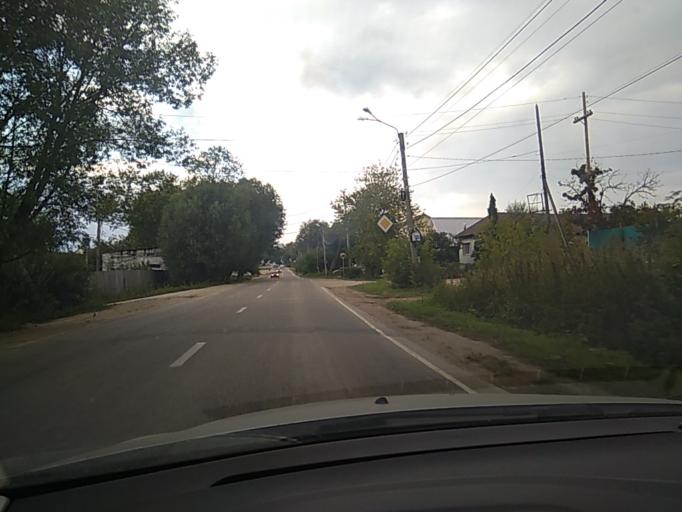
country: RU
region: Chelyabinsk
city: Kyshtym
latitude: 55.6982
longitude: 60.5524
